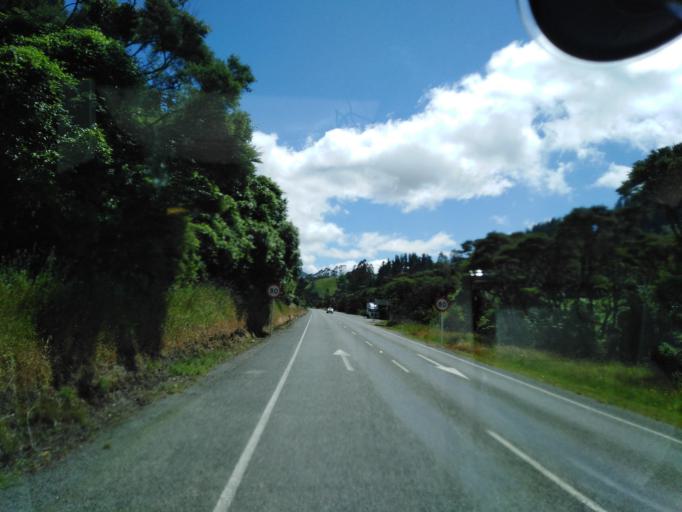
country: NZ
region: Nelson
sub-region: Nelson City
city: Nelson
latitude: -41.2240
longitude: 173.3965
